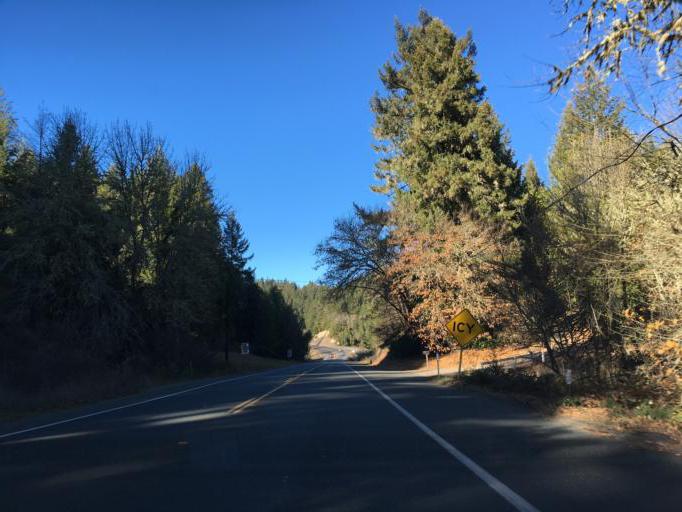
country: US
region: California
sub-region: Mendocino County
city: Brooktrails
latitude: 39.4608
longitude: -123.3498
